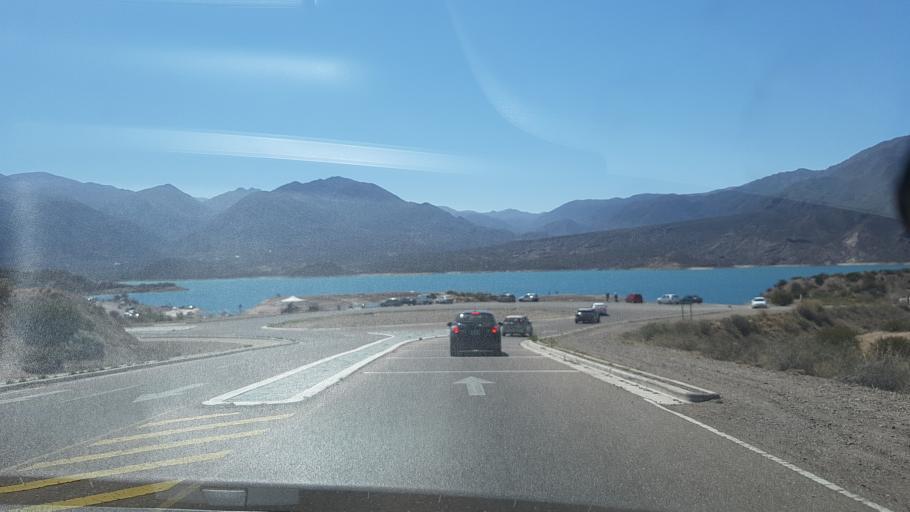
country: AR
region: Mendoza
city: Lujan de Cuyo
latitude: -32.9896
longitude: -69.1665
